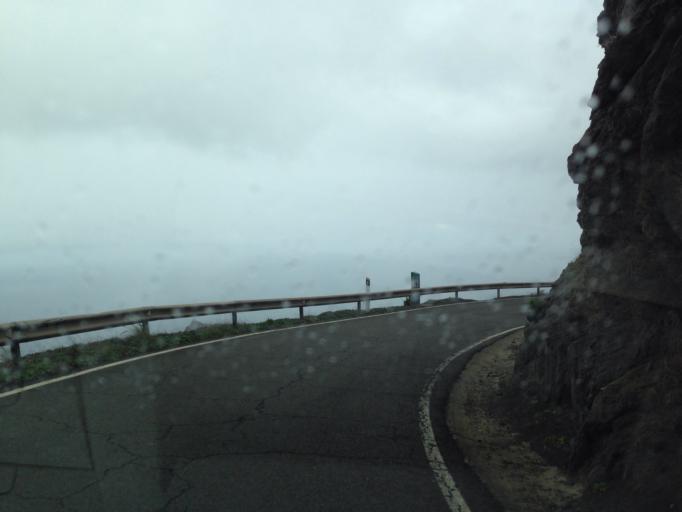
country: ES
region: Canary Islands
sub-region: Provincia de Las Palmas
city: San Nicolas
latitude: 28.0359
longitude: -15.7540
